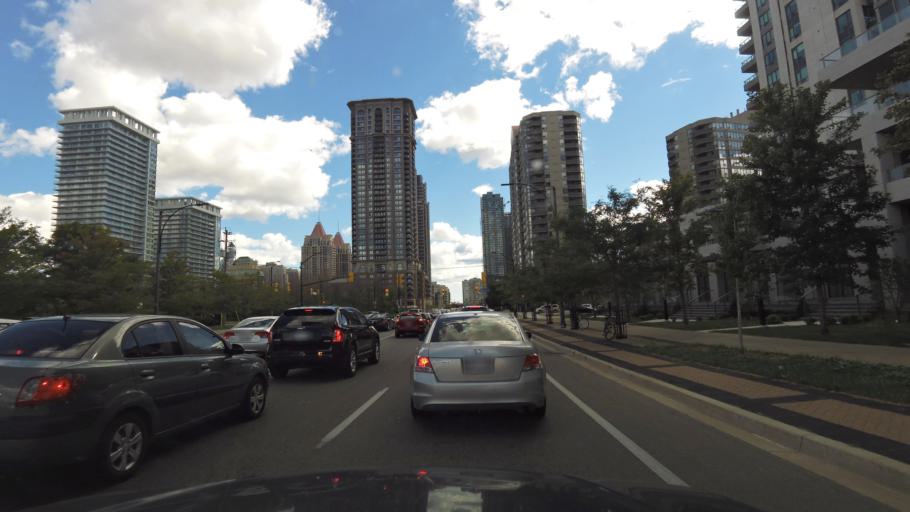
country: CA
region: Ontario
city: Mississauga
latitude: 43.5903
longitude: -79.6523
